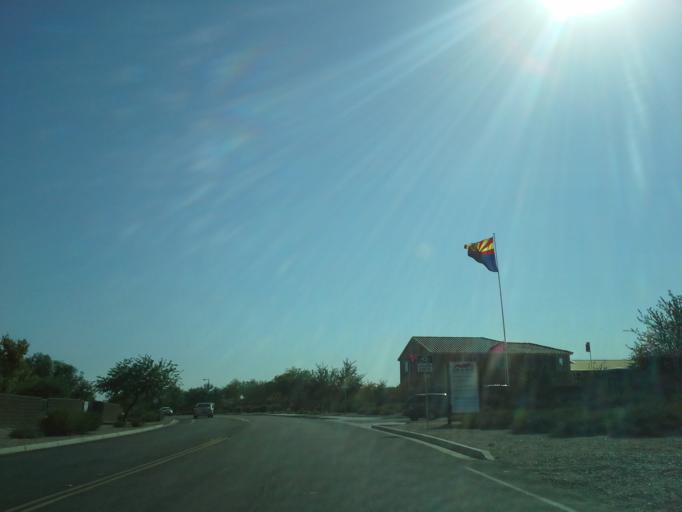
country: US
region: Arizona
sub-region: Pinal County
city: San Tan Valley
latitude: 33.1453
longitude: -111.5525
